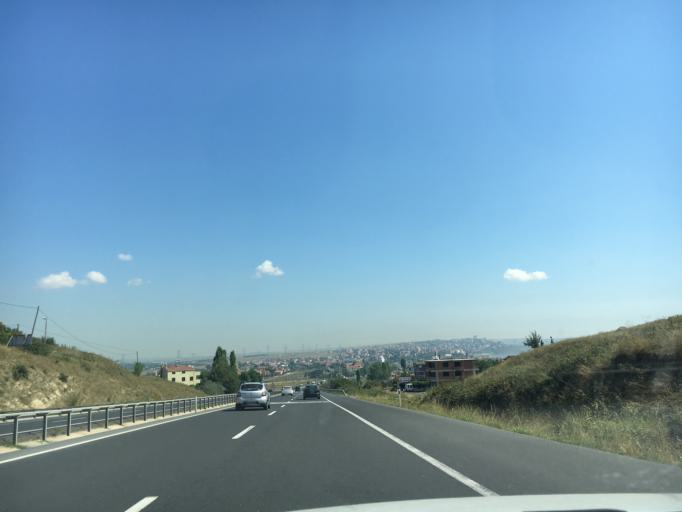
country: TR
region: Tekirdag
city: Sultankoy
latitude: 41.0024
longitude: 27.9764
